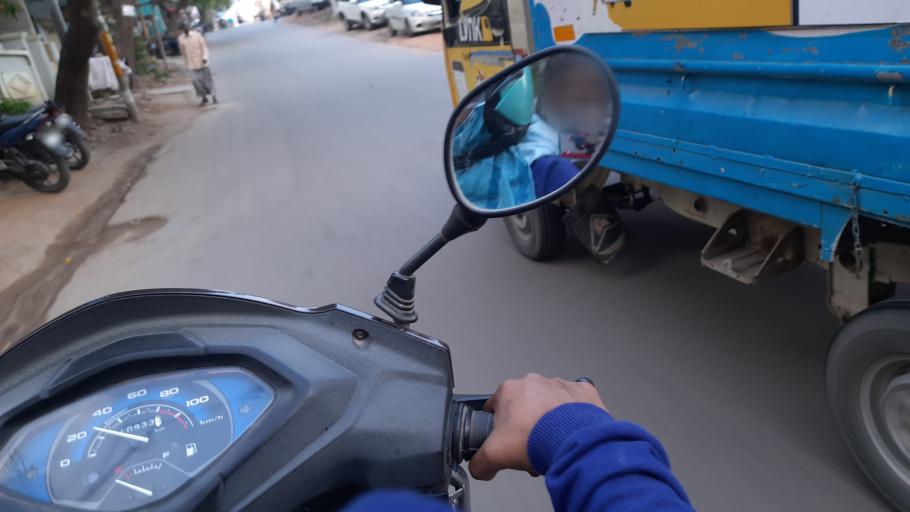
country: IN
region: Telangana
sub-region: Rangareddi
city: Kukatpalli
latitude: 17.4938
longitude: 78.4253
